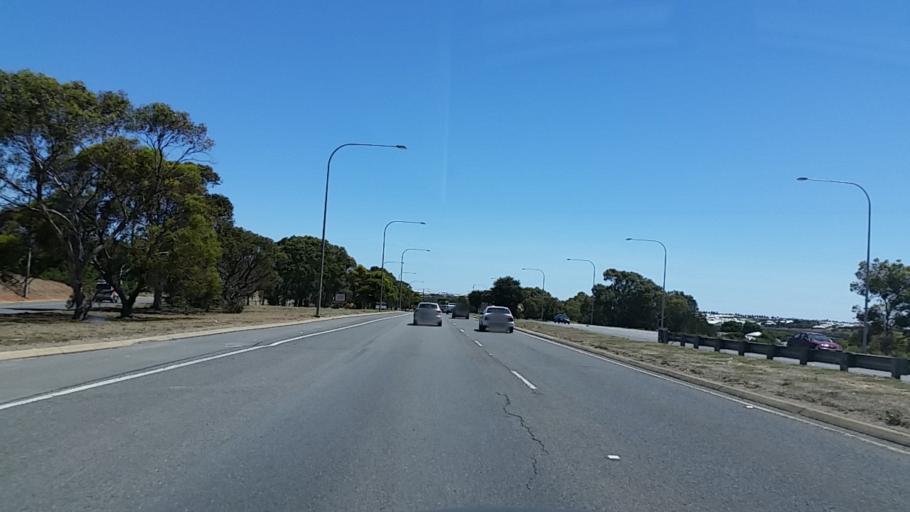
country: AU
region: South Australia
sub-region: Onkaparinga
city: Noarlunga
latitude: -35.1675
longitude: 138.5066
